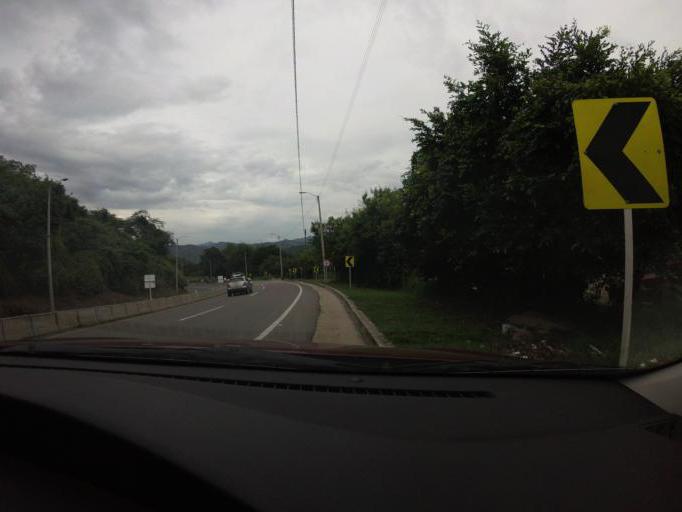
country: CO
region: Cundinamarca
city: Villeta
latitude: 5.0122
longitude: -74.4796
